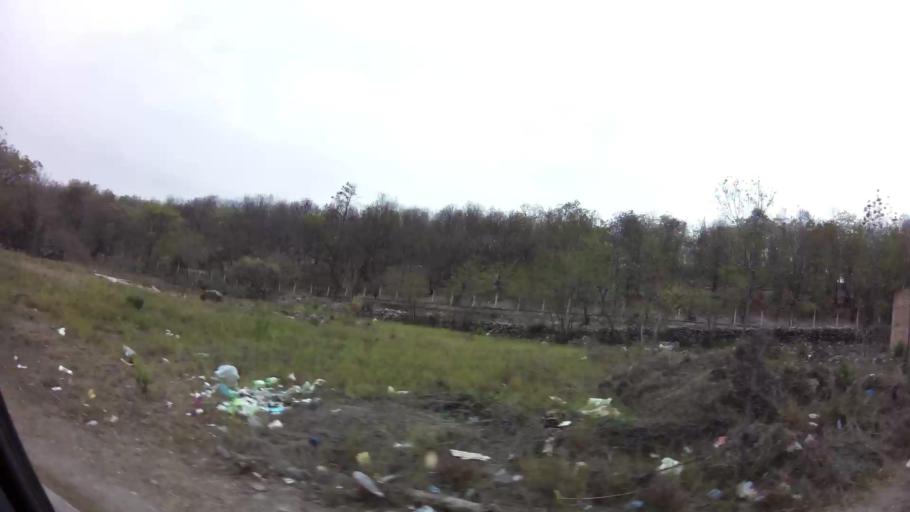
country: HN
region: Francisco Morazan
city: Tegucigalpa
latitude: 14.0696
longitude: -87.2443
